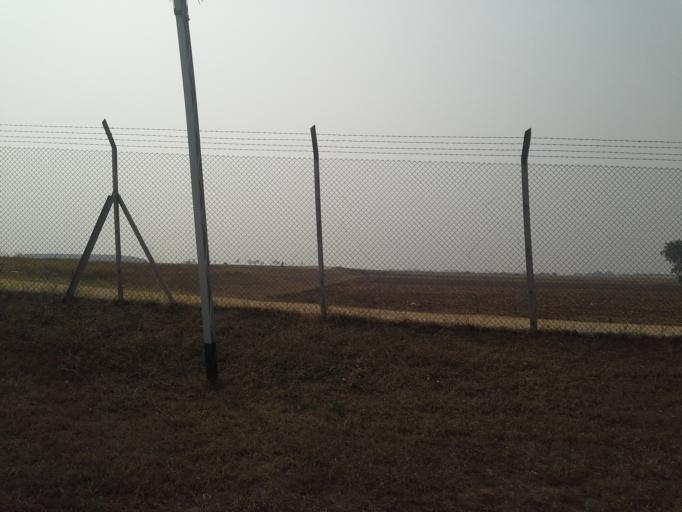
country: IN
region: Telangana
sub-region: Medak
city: Patancheru
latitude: 17.5097
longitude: 78.2739
